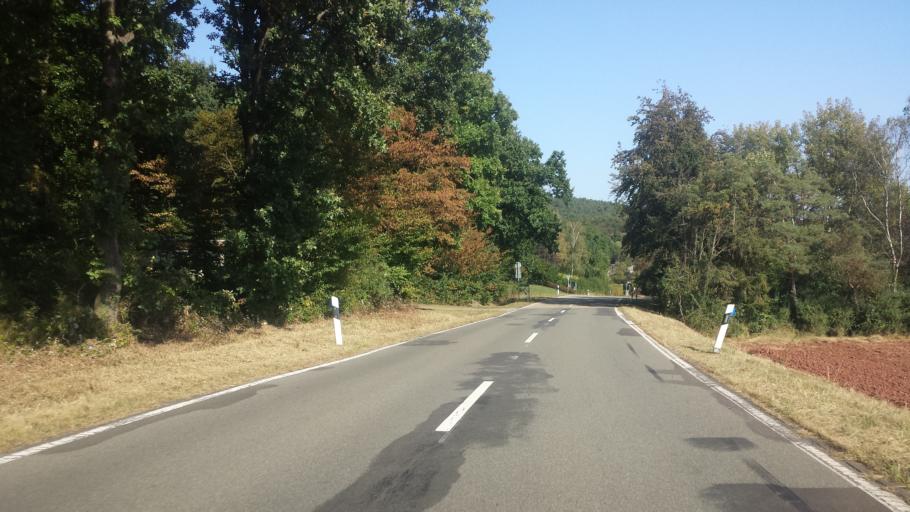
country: DE
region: Rheinland-Pfalz
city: Kerzenheim
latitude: 49.5566
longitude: 8.0369
